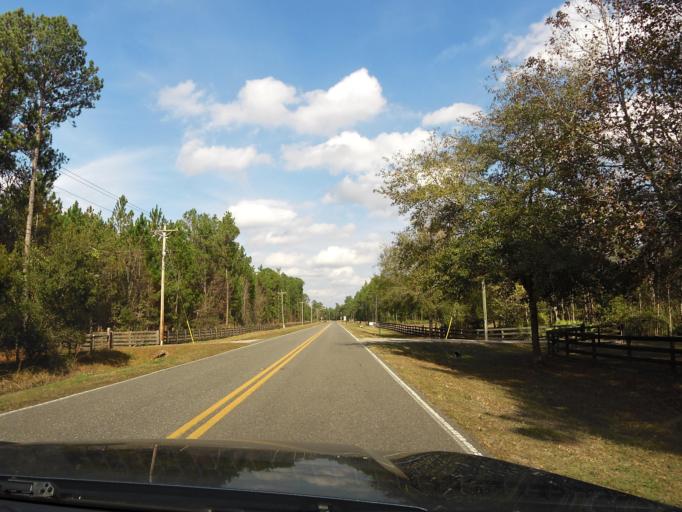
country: US
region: Florida
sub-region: Duval County
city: Baldwin
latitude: 30.1545
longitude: -82.0023
